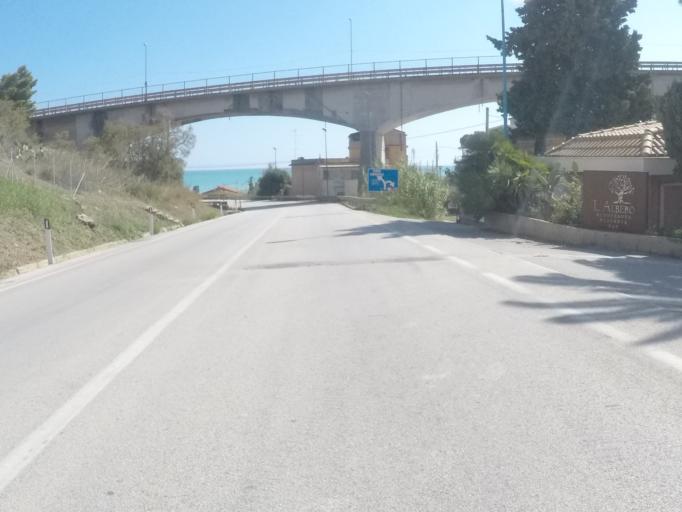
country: IT
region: Sicily
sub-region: Agrigento
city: Porto Empedocle
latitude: 37.2949
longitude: 13.5016
